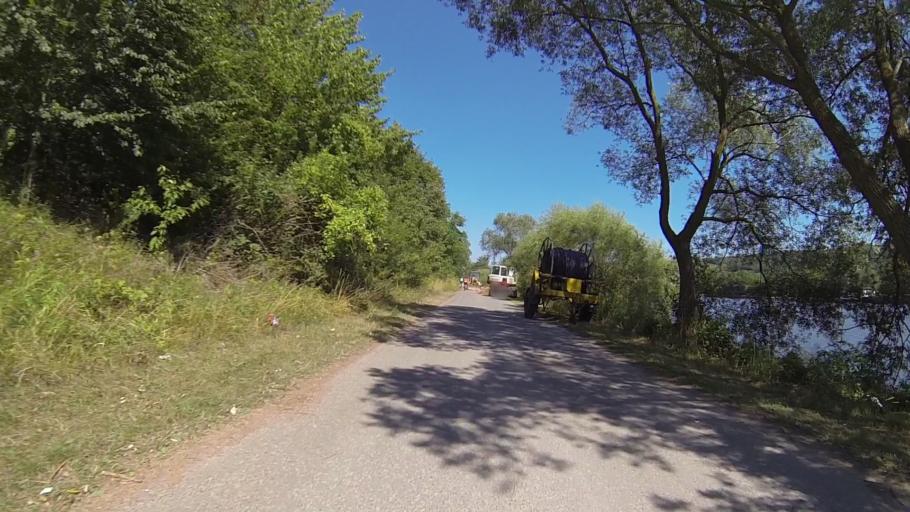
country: DE
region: Rheinland-Pfalz
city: Konz
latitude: 49.7105
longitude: 6.5816
